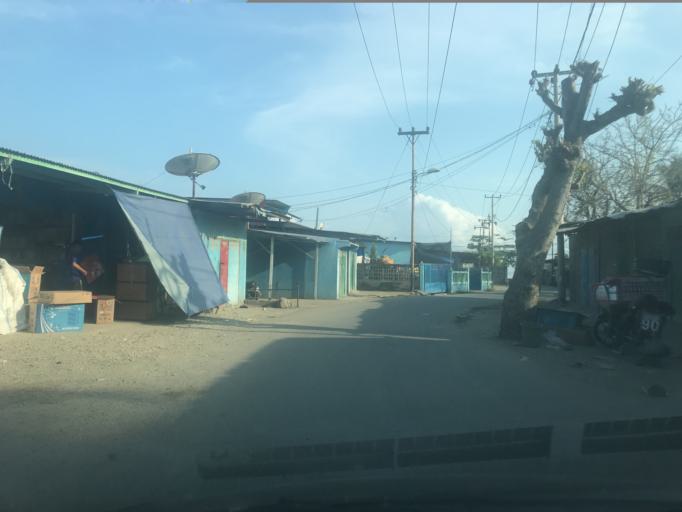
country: TL
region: Dili
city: Dili
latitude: -8.5493
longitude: 125.5607
